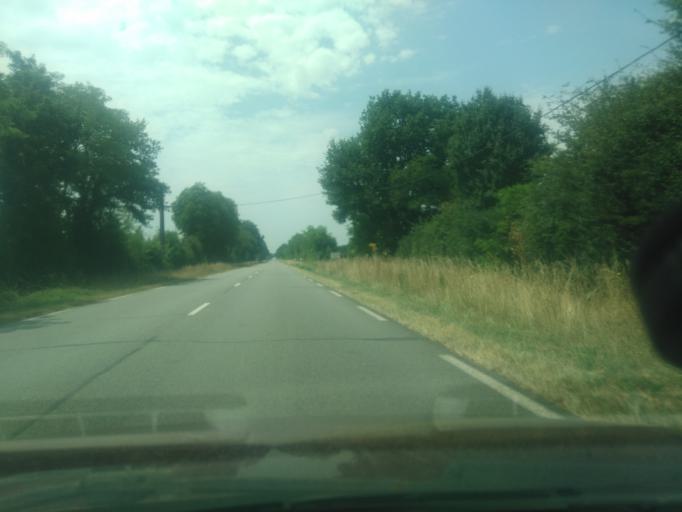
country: FR
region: Centre
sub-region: Departement de l'Indre
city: Le Blanc
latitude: 46.6183
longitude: 1.0233
